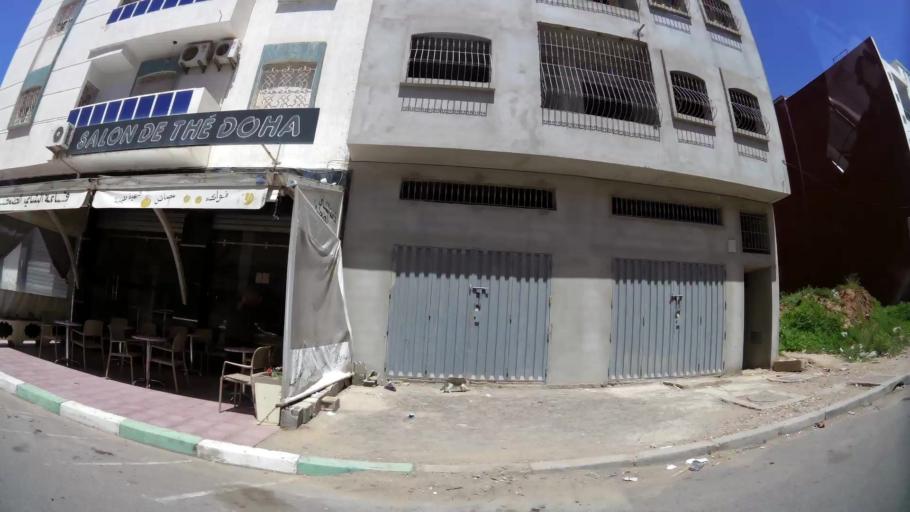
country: MA
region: Oued ed Dahab-Lagouira
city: Dakhla
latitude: 30.4288
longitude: -9.5551
